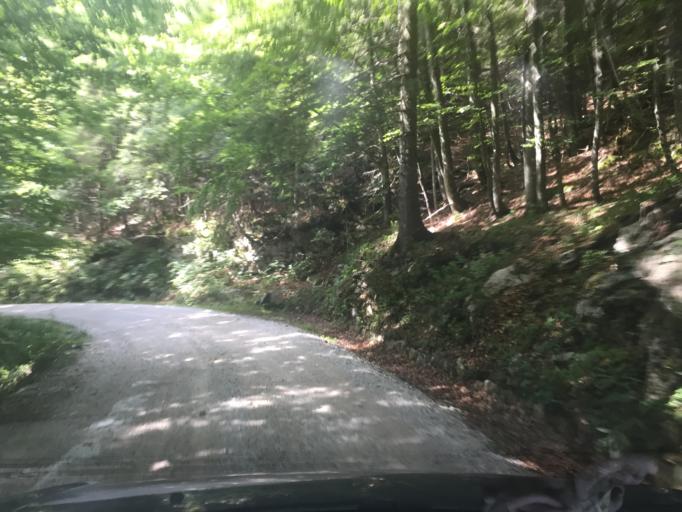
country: SI
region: Ajdovscina
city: Lokavec
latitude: 45.9876
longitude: 13.8378
